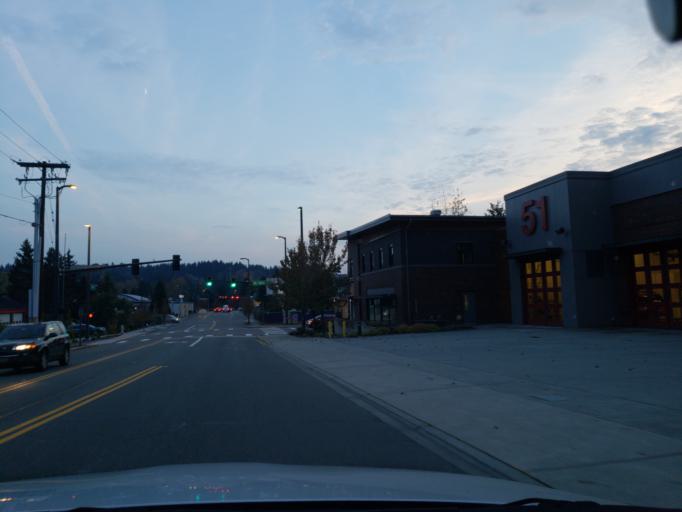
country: US
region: Washington
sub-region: King County
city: Kenmore
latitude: 47.7597
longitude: -122.2438
